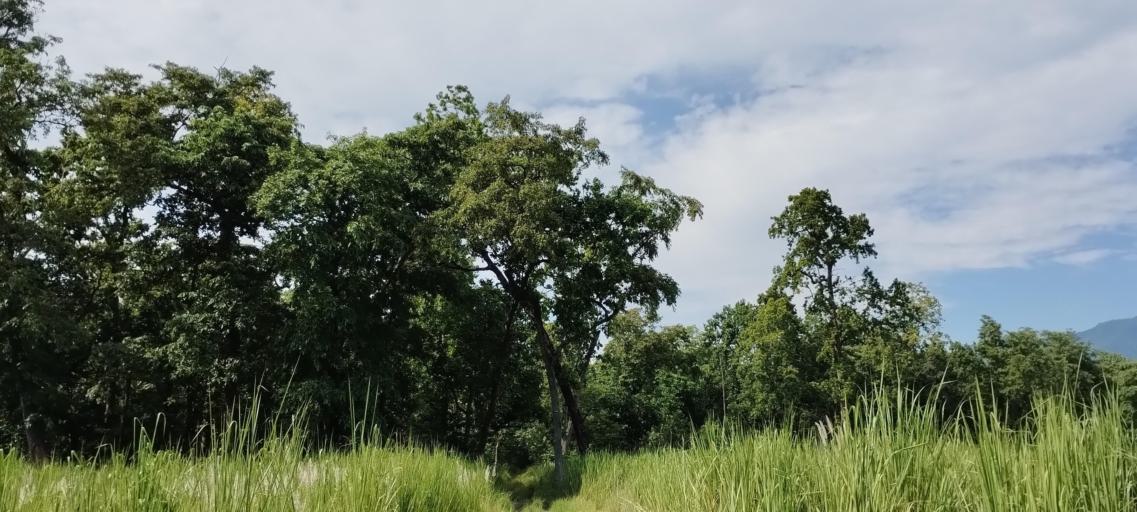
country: NP
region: Far Western
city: Tikapur
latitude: 28.5605
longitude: 81.2949
